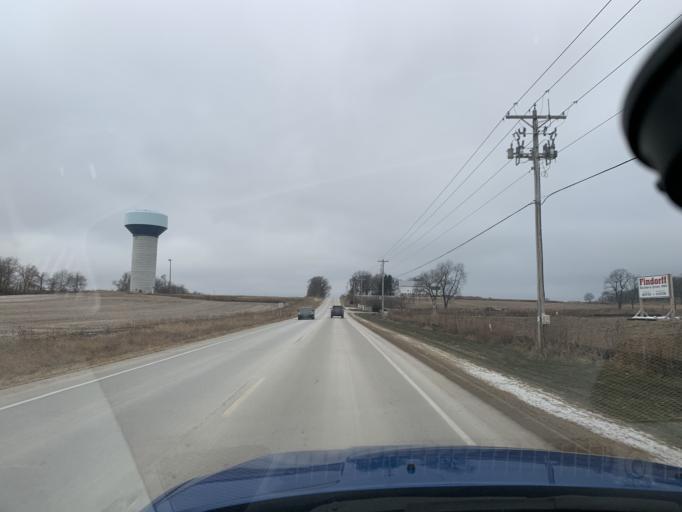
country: US
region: Wisconsin
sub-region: Dane County
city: Middleton
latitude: 43.0748
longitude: -89.5639
